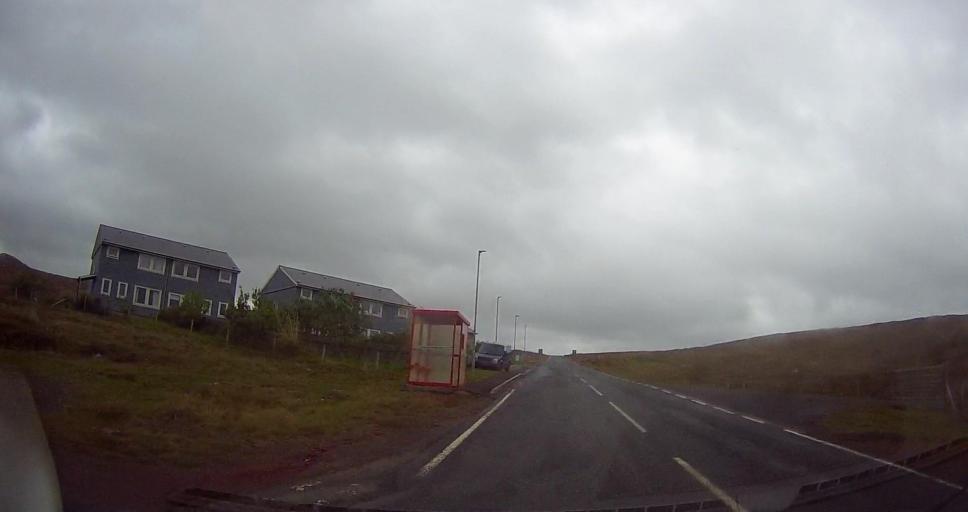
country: GB
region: Scotland
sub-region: Shetland Islands
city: Lerwick
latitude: 60.4876
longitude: -1.4501
